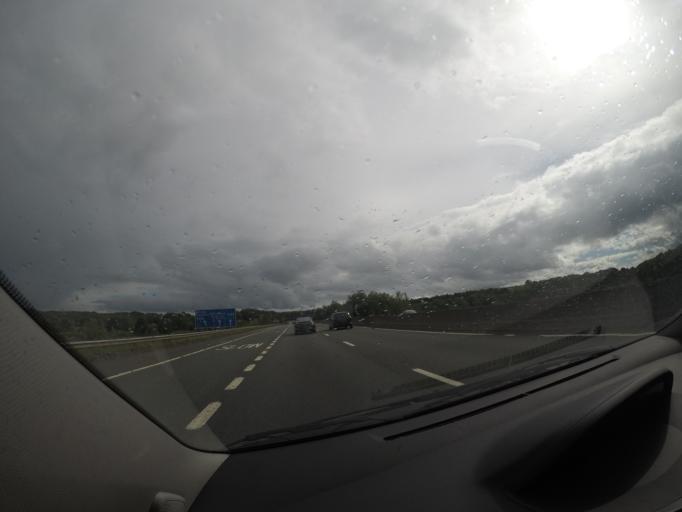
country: GB
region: Scotland
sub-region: Falkirk
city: Dunipace
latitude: 55.9873
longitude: -3.9438
